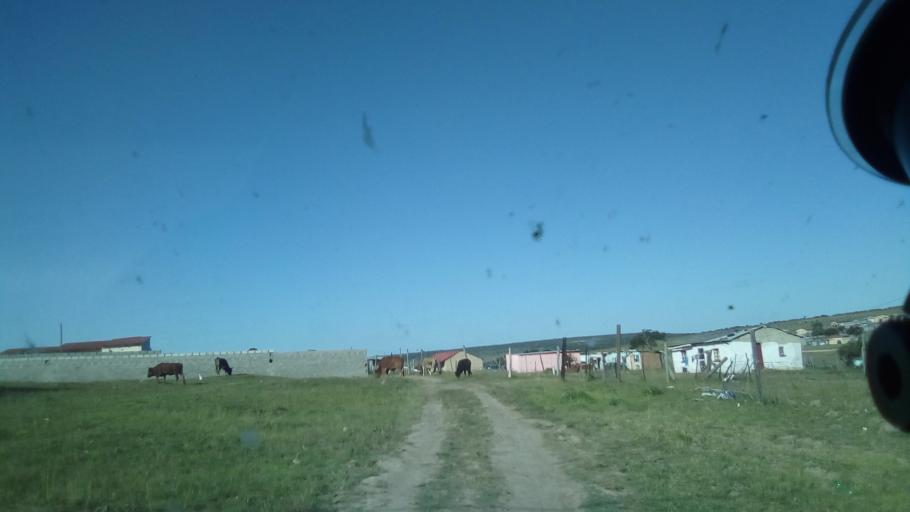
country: ZA
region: Eastern Cape
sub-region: Buffalo City Metropolitan Municipality
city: Bhisho
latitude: -32.8282
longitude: 27.3702
